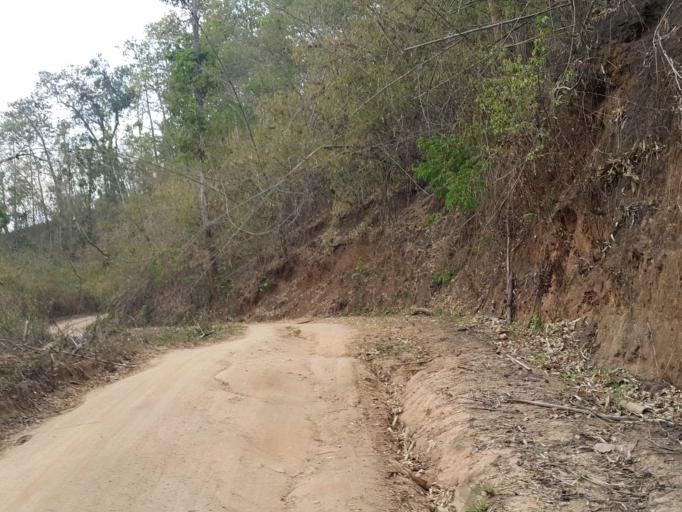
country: TH
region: Chiang Mai
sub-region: Amphoe Chiang Dao
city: Chiang Dao
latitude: 19.2818
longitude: 98.7626
